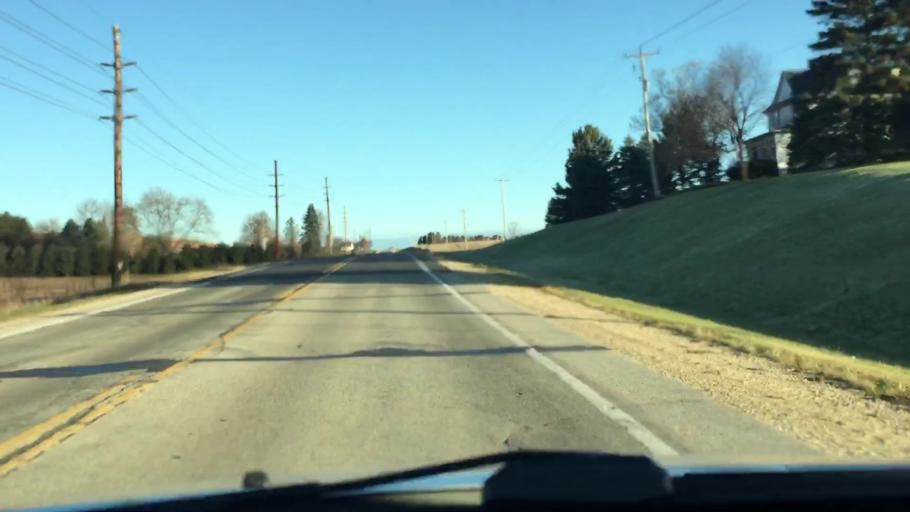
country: US
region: Wisconsin
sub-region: Washington County
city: Hartford
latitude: 43.3598
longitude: -88.4580
